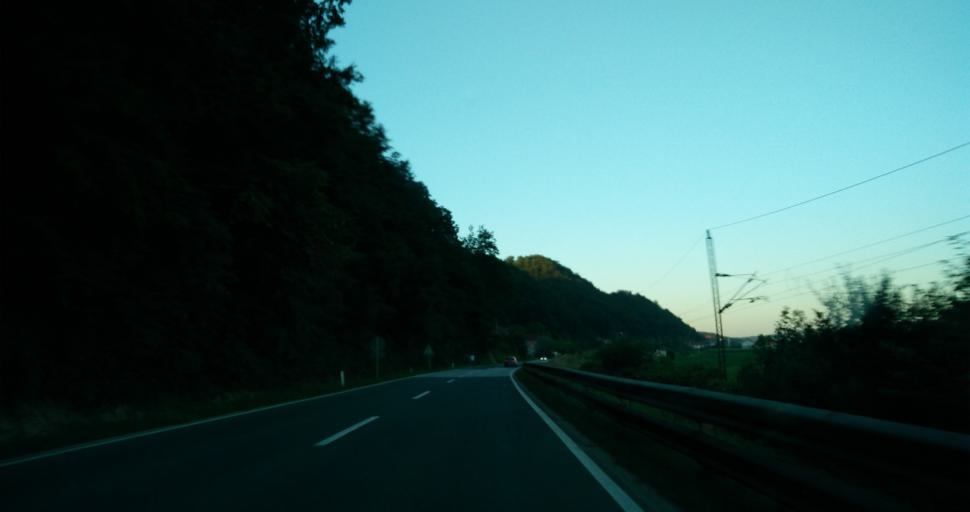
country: BA
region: Republika Srpska
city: Bosanski Novi
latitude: 45.0424
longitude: 16.4507
